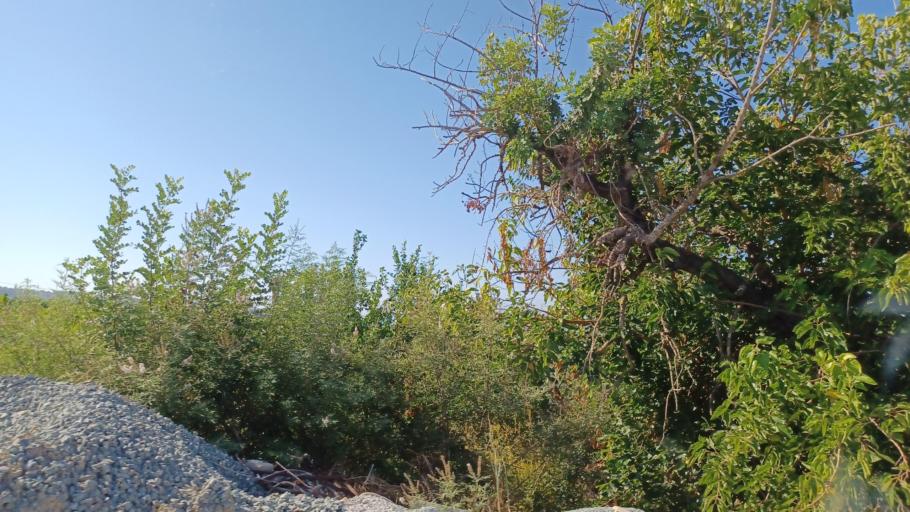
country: CY
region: Pafos
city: Kissonerga
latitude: 34.8492
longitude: 32.3901
